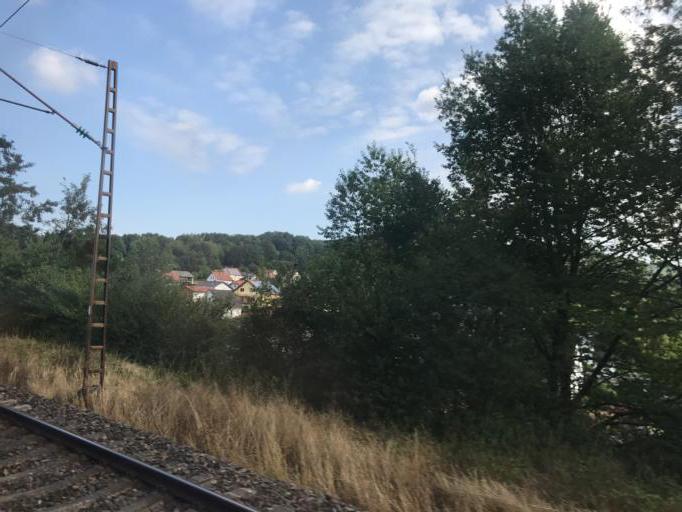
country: DE
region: Saarland
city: Namborn
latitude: 49.5106
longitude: 7.1621
